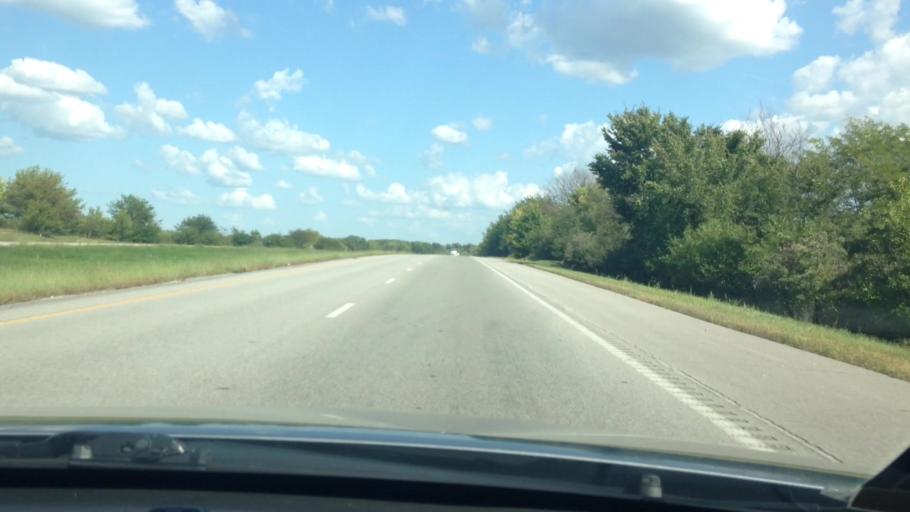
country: US
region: Missouri
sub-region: Clay County
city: Smithville
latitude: 39.3108
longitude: -94.5318
